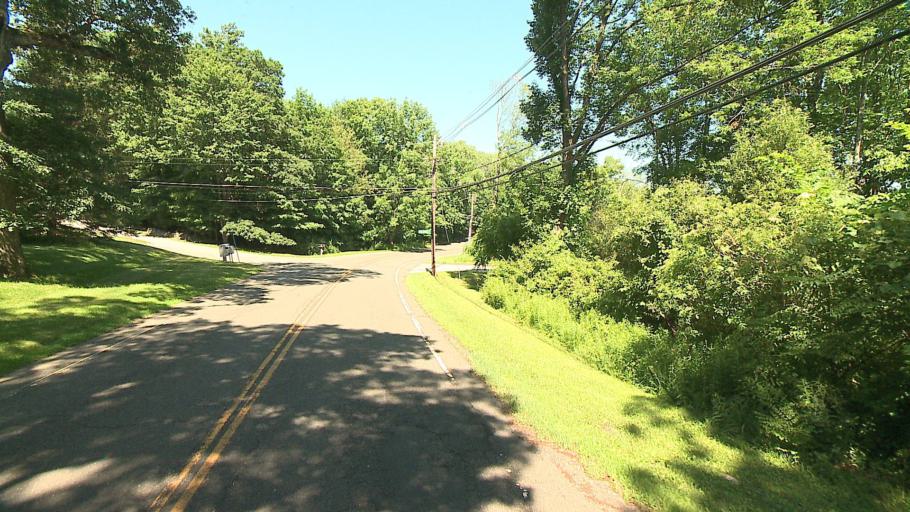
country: US
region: Connecticut
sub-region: Fairfield County
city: Ridgefield
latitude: 41.2848
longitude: -73.5166
